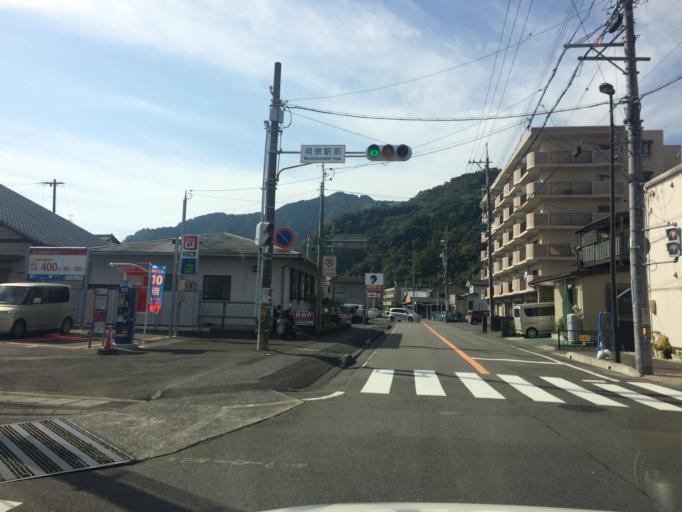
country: JP
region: Shizuoka
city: Shizuoka-shi
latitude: 34.9222
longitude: 138.3608
